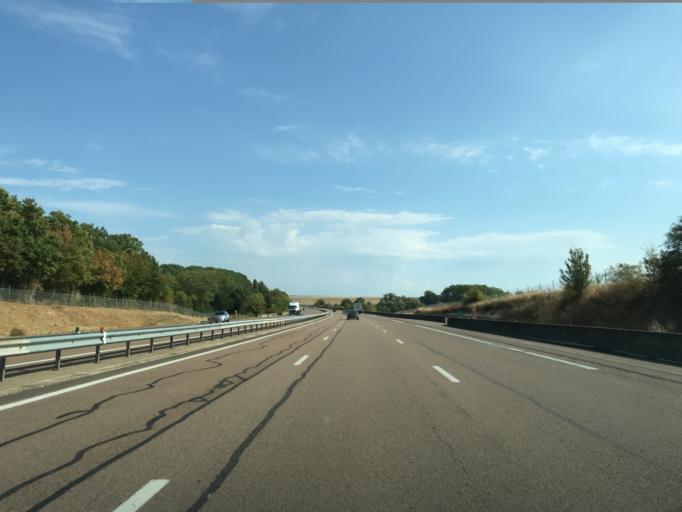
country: FR
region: Bourgogne
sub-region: Departement de l'Yonne
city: Aillant-sur-Tholon
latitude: 47.9035
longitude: 3.3472
